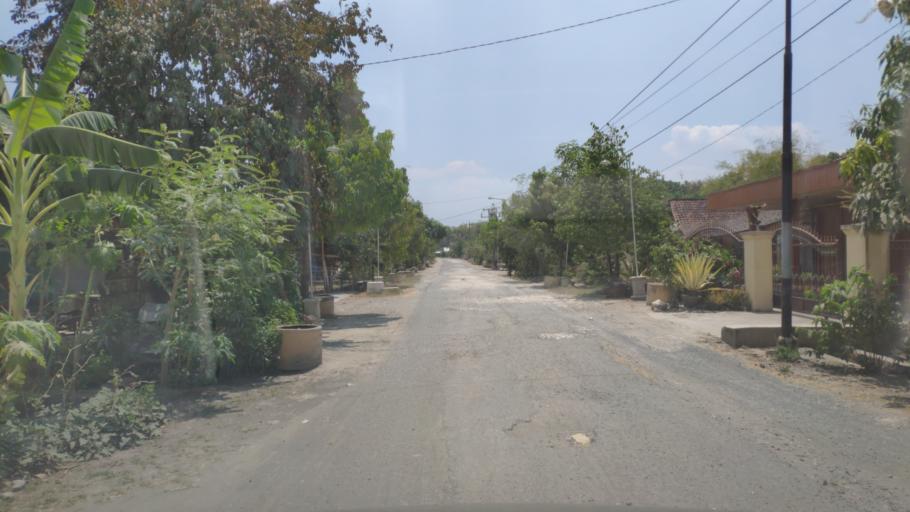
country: ID
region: Central Java
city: Kemantren
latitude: -7.2104
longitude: 111.5206
